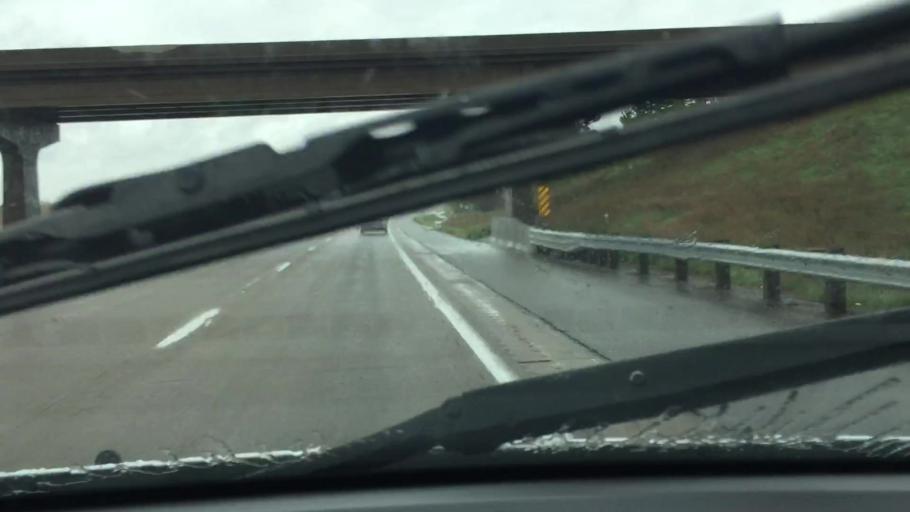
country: US
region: Iowa
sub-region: Poweshiek County
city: Brooklyn
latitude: 41.6947
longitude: -92.5030
